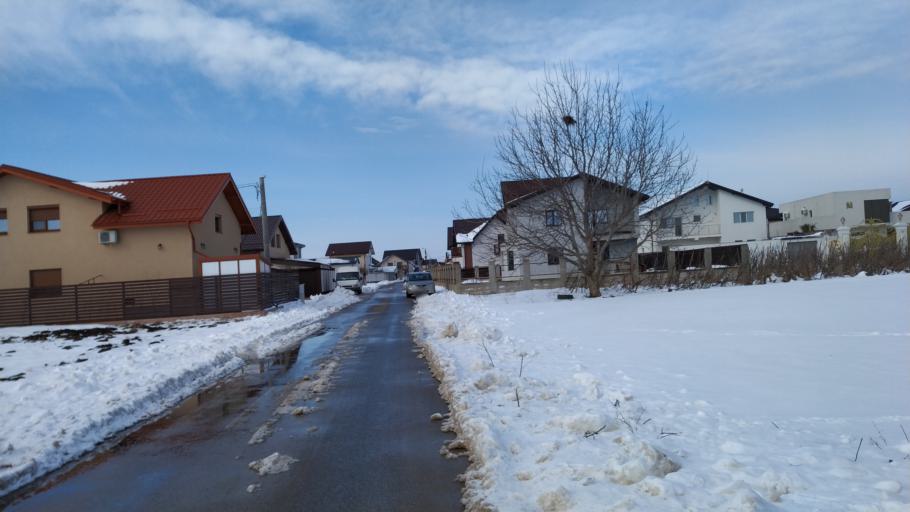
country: RO
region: Ilfov
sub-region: Comuna Berceni
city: Berceni
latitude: 44.3226
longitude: 26.1910
